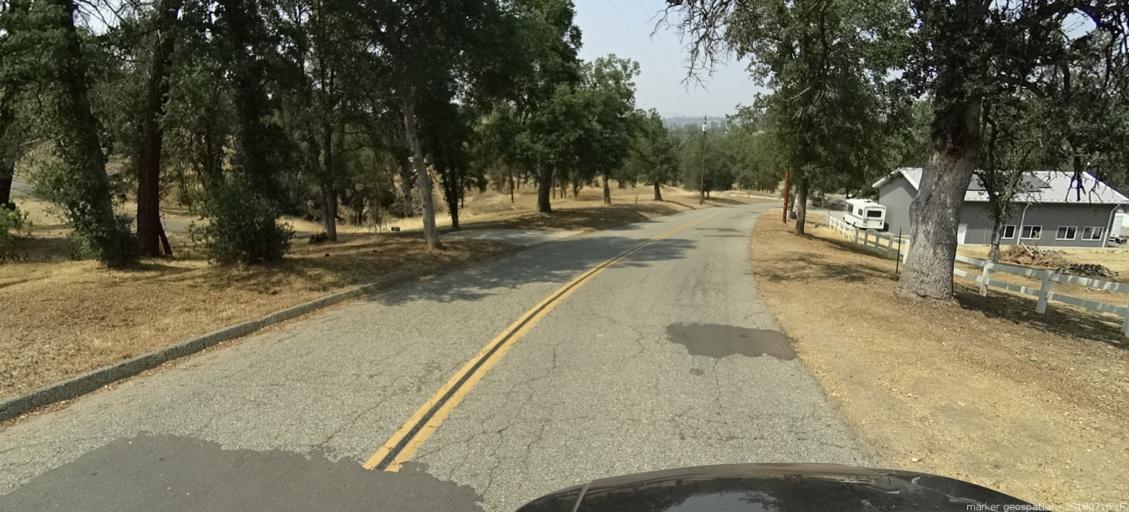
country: US
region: California
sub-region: Madera County
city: Yosemite Lakes
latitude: 37.2236
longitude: -119.7781
